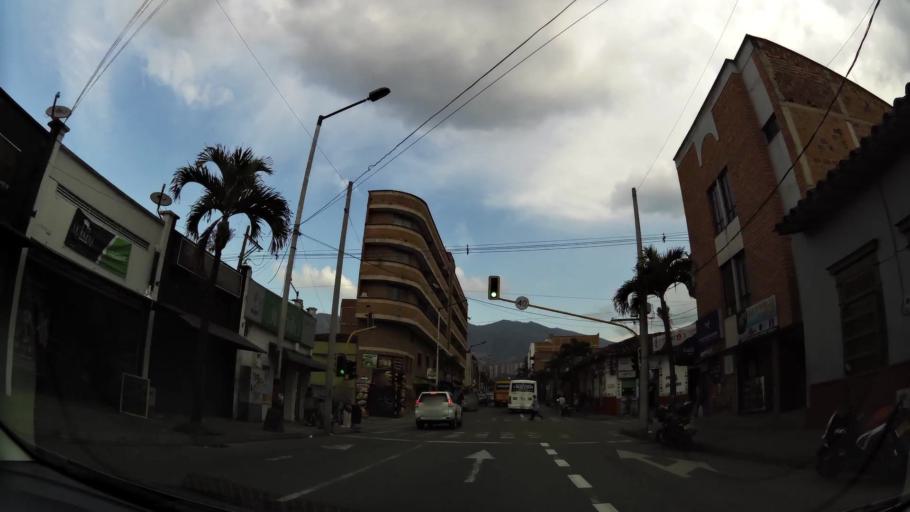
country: CO
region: Antioquia
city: Envigado
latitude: 6.1684
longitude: -75.5884
